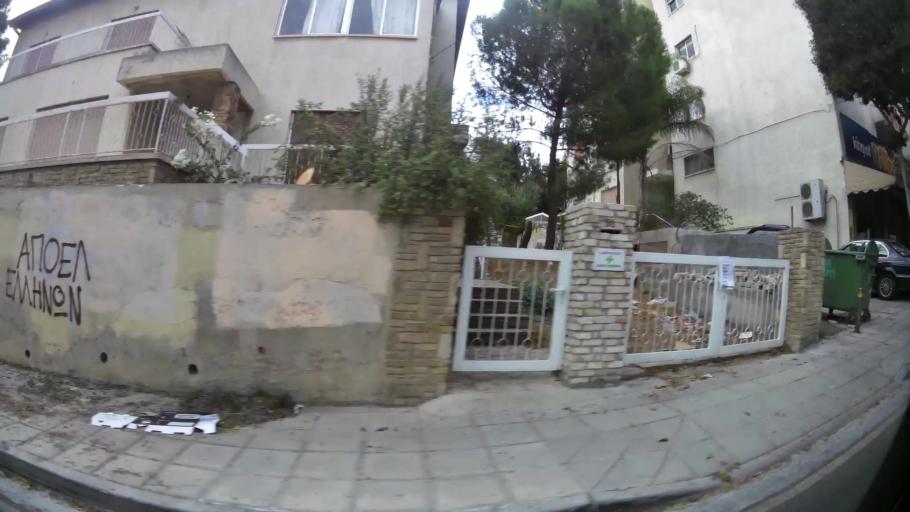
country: CY
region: Lefkosia
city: Nicosia
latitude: 35.1579
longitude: 33.3659
